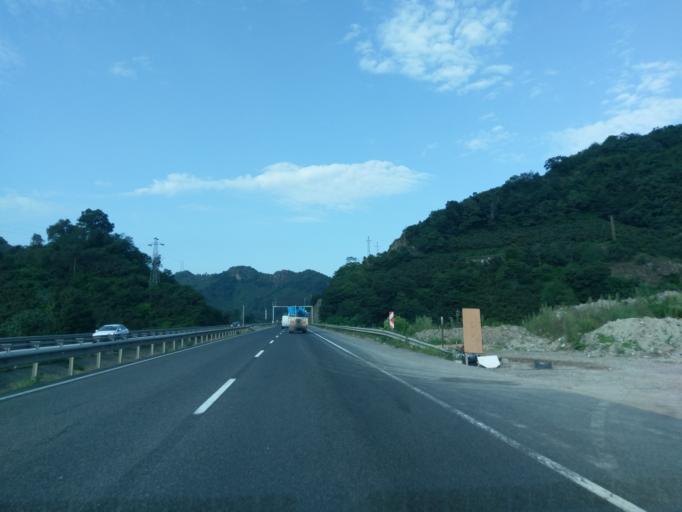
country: TR
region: Ordu
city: Ordu
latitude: 40.9879
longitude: 37.7973
